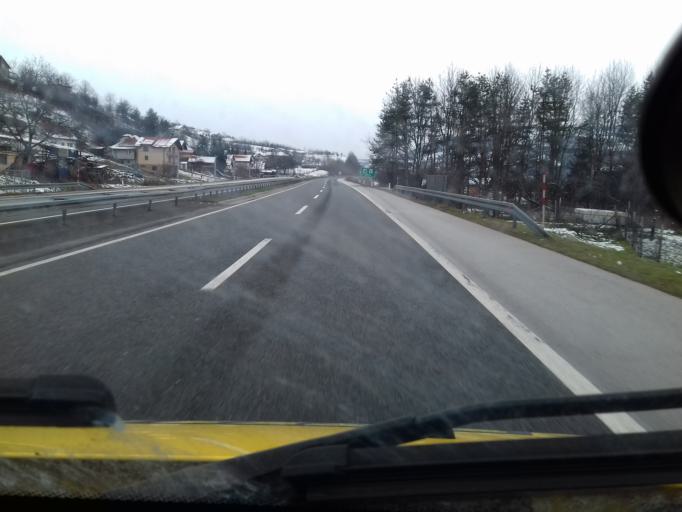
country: BA
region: Federation of Bosnia and Herzegovina
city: Visoko
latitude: 43.9967
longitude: 18.1862
